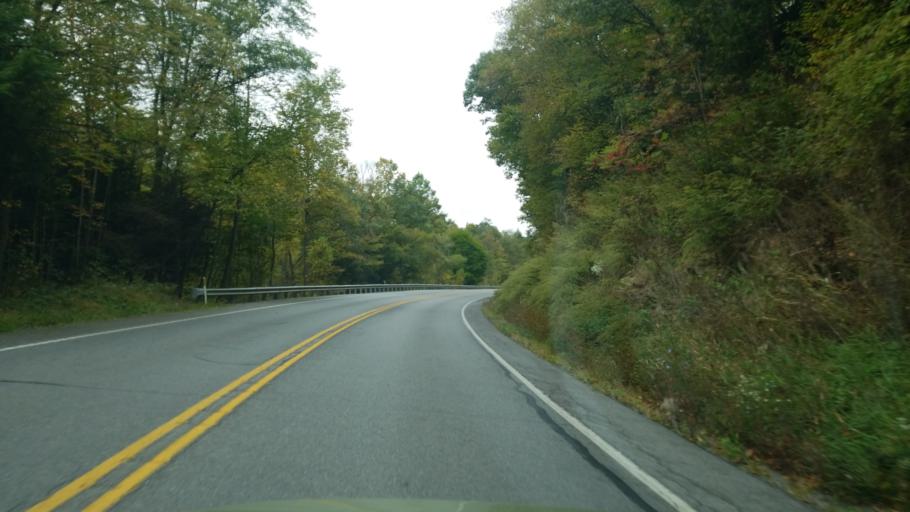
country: US
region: Pennsylvania
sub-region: Clearfield County
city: Curwensville
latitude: 40.9702
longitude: -78.5575
